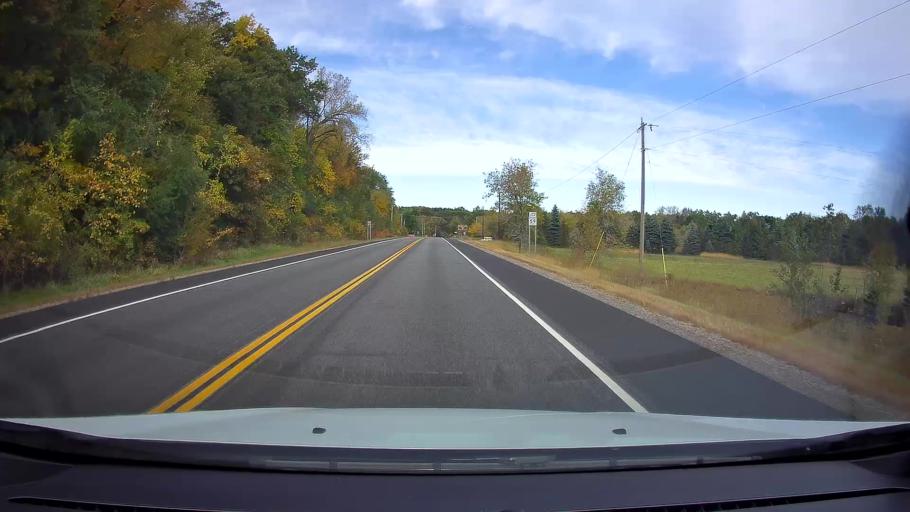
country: US
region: Wisconsin
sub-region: Saint Croix County
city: Somerset
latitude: 45.1414
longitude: -92.7594
